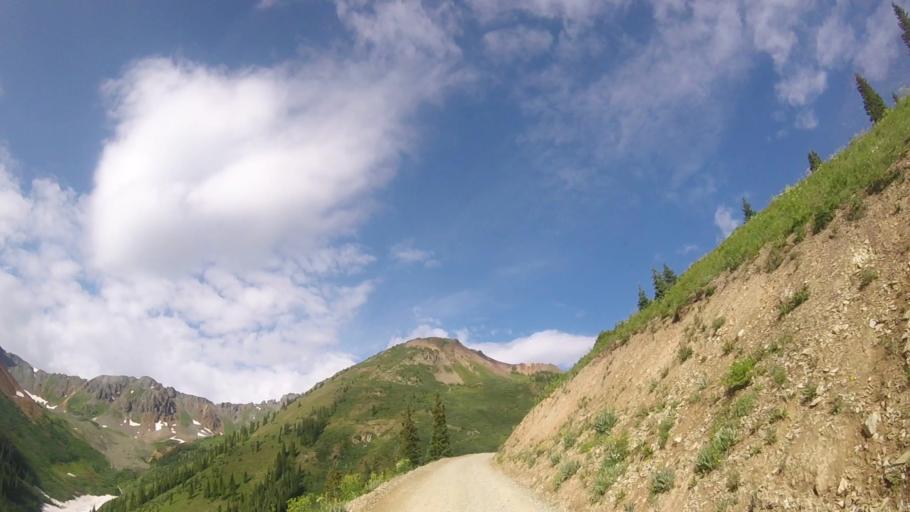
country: US
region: Colorado
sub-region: San Miguel County
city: Telluride
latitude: 37.8459
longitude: -107.7650
